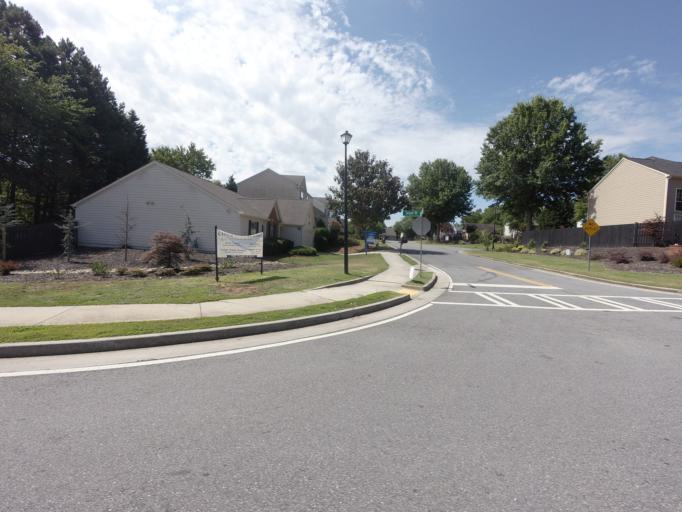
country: US
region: Georgia
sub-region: Fulton County
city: Johns Creek
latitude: 34.0698
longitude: -84.1809
